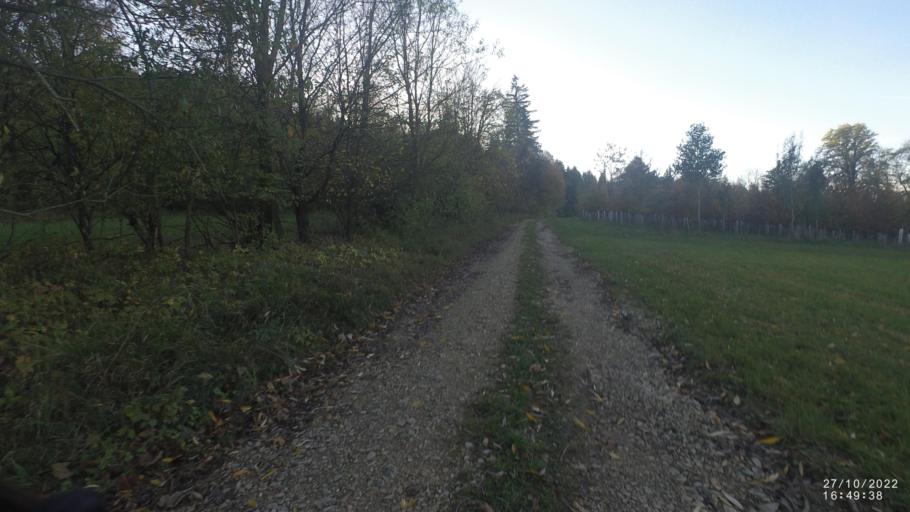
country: DE
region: Baden-Wuerttemberg
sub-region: Regierungsbezirk Stuttgart
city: Gingen an der Fils
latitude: 48.6458
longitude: 9.7602
